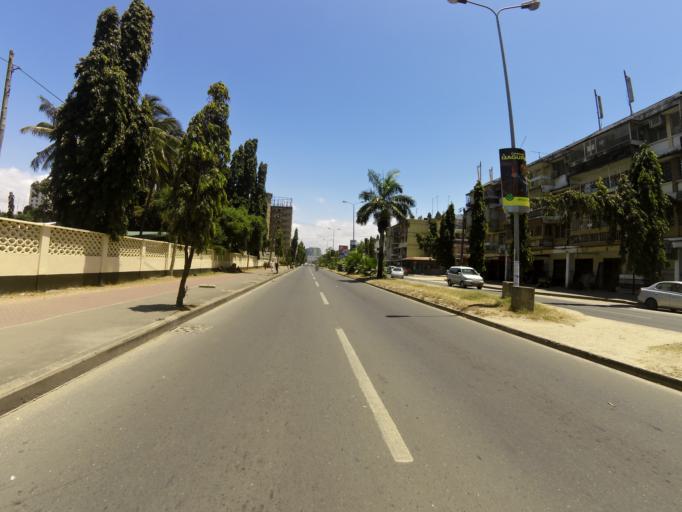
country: TZ
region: Dar es Salaam
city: Dar es Salaam
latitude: -6.8130
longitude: 39.2838
